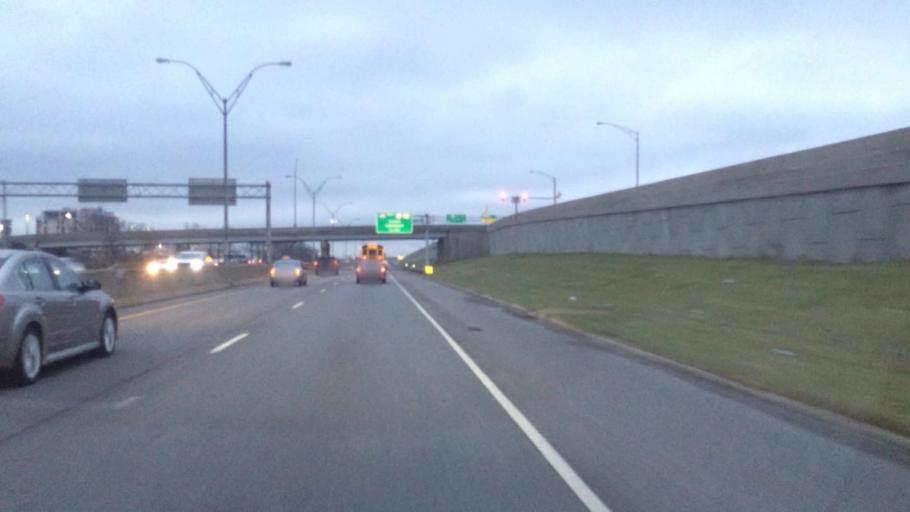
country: US
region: Ohio
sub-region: Cuyahoga County
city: Brook Park
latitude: 41.4065
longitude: -81.8351
